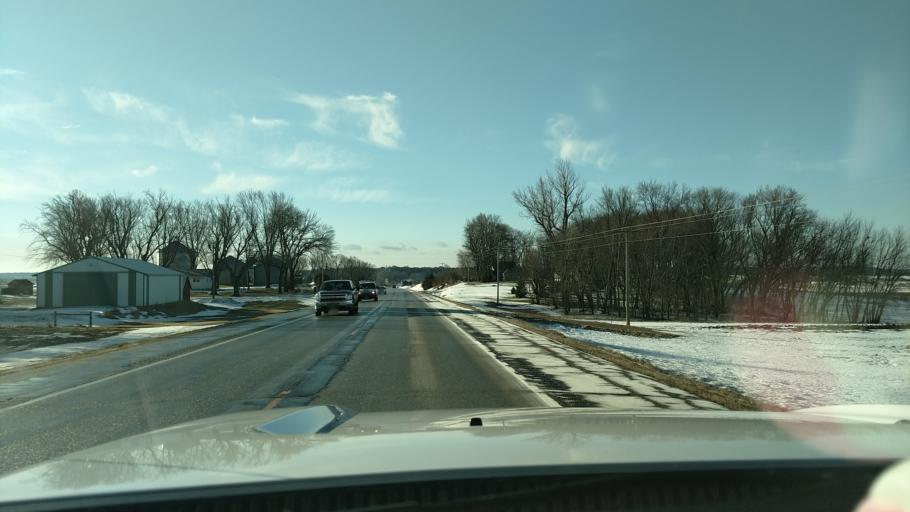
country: US
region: Minnesota
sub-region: Olmsted County
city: Oronoco
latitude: 44.1592
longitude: -92.4193
